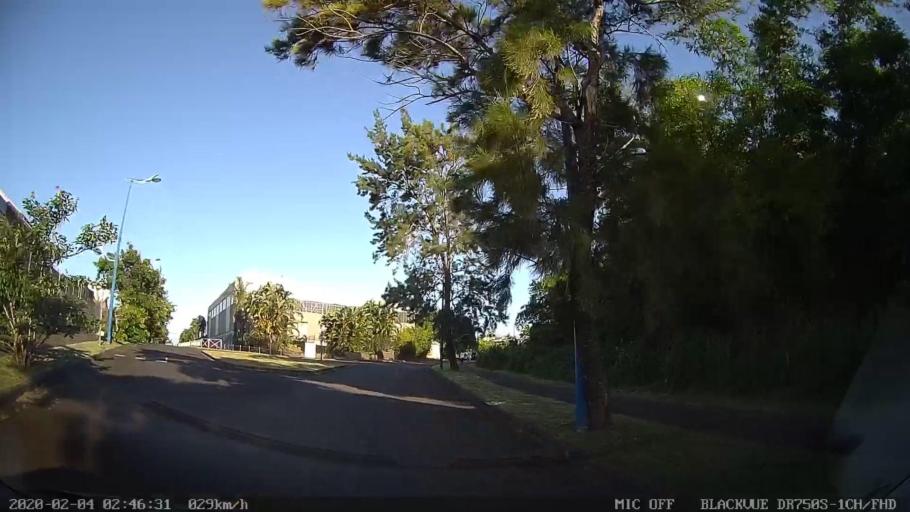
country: RE
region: Reunion
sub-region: Reunion
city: Sainte-Marie
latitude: -20.9240
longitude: 55.5266
